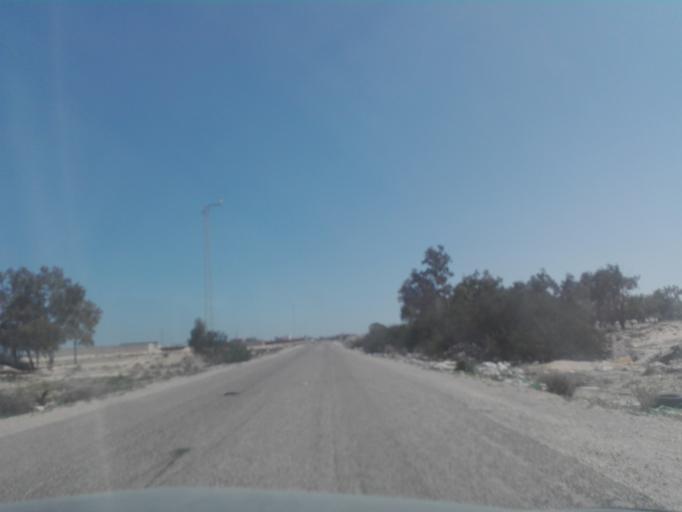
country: TN
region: Qabis
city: Gabes
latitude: 33.8713
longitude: 10.0394
